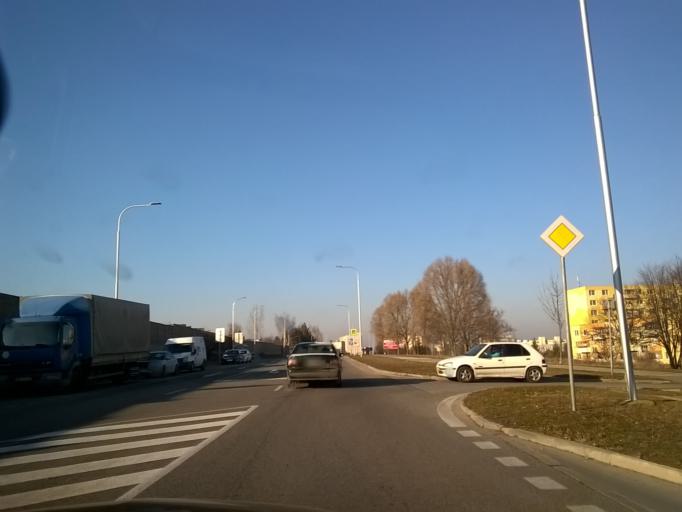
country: SK
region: Nitriansky
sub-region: Okres Nitra
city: Nitra
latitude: 48.2985
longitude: 18.0540
